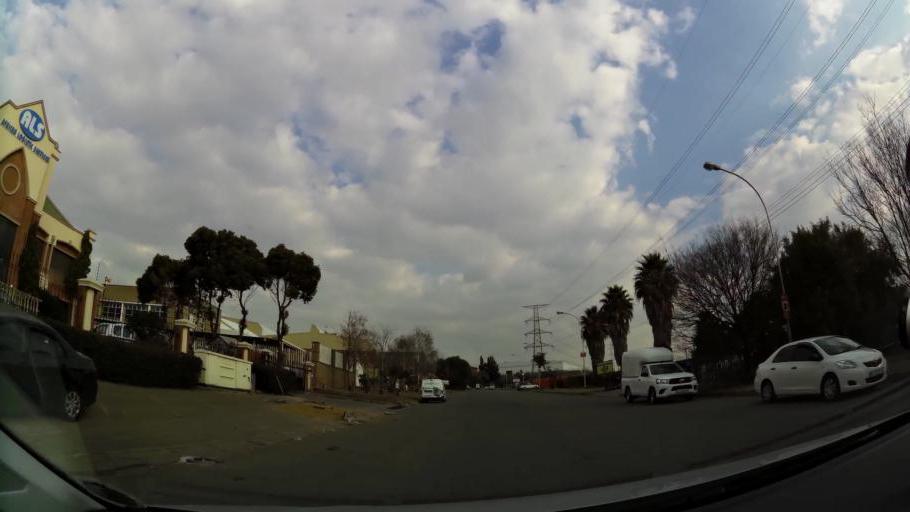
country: ZA
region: Gauteng
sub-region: City of Johannesburg Metropolitan Municipality
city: Modderfontein
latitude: -26.1502
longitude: 28.1819
